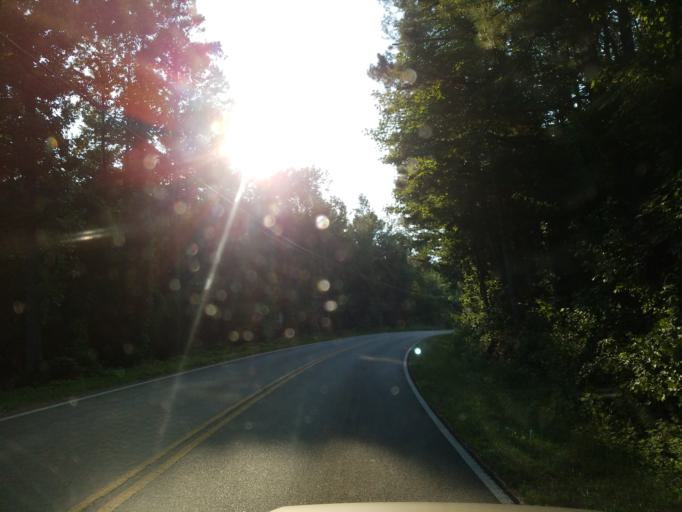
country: US
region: Georgia
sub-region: Pickens County
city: Jasper
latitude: 34.5407
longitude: -84.5395
